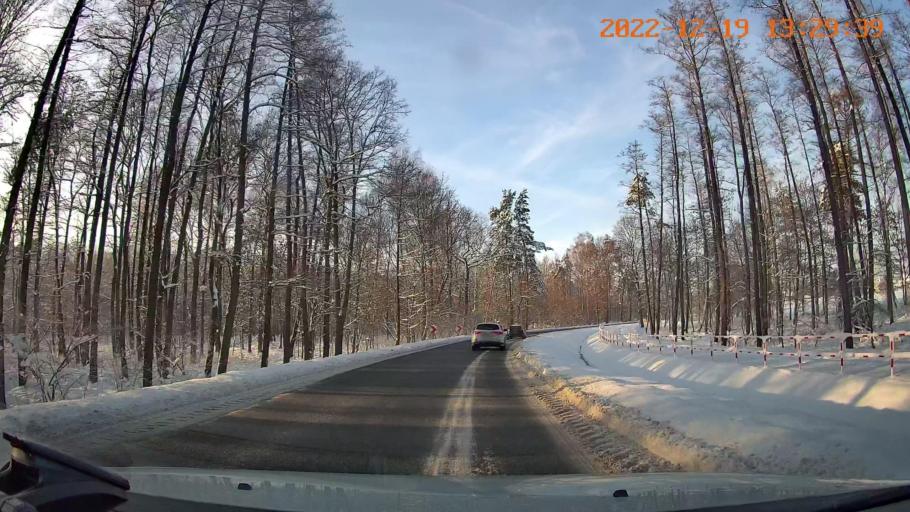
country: PL
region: Silesian Voivodeship
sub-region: Powiat bierunsko-ledzinski
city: Ledziny
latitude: 50.1153
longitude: 19.1170
